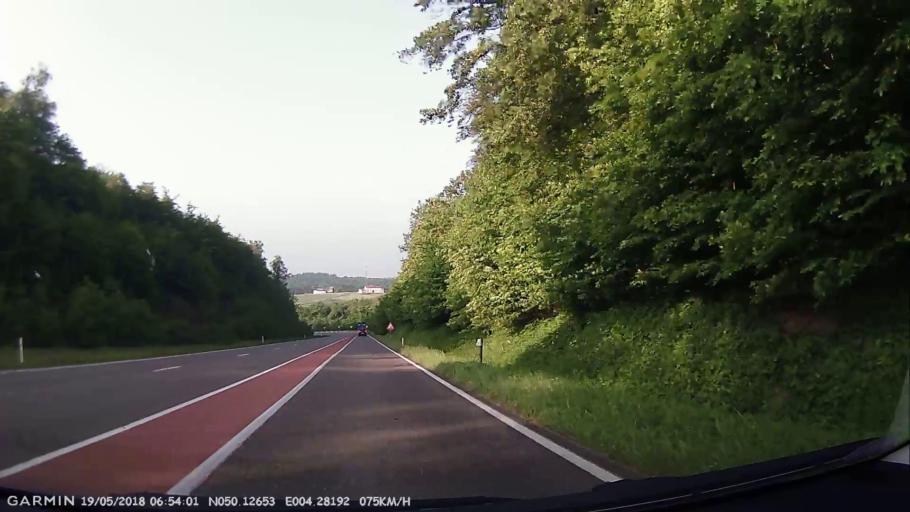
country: BE
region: Wallonia
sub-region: Province du Hainaut
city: Froidchapelle
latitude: 50.1263
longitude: 4.2818
